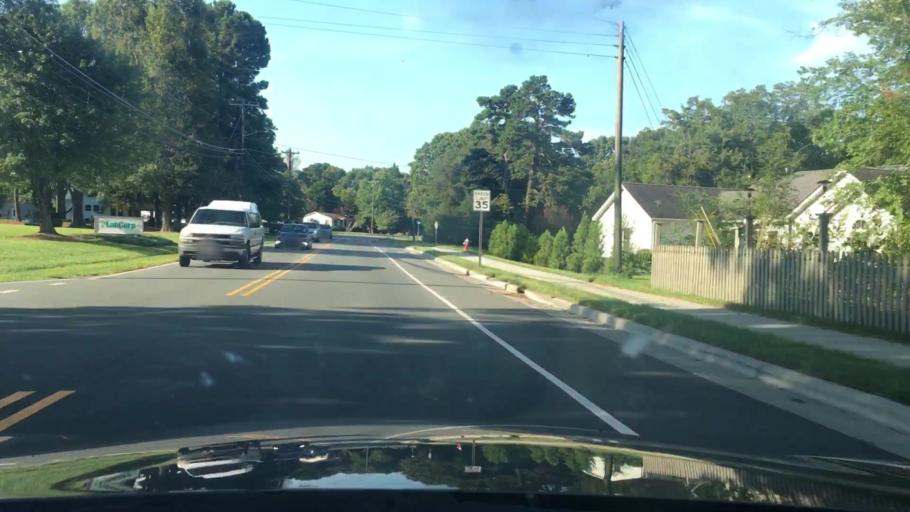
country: US
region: North Carolina
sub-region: Alamance County
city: Elon
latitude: 36.0946
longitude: -79.5086
